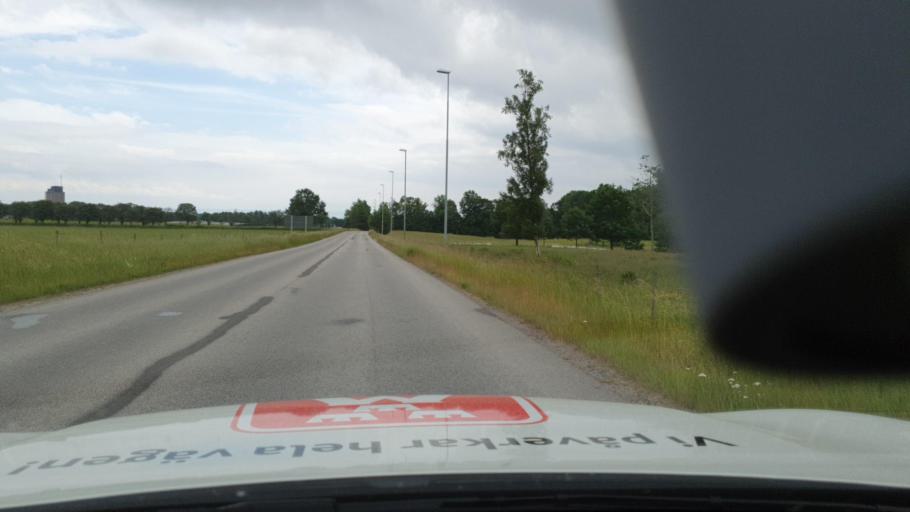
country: SE
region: Vaestra Goetaland
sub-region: Hjo Kommun
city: Hjo
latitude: 58.3186
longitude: 14.2702
